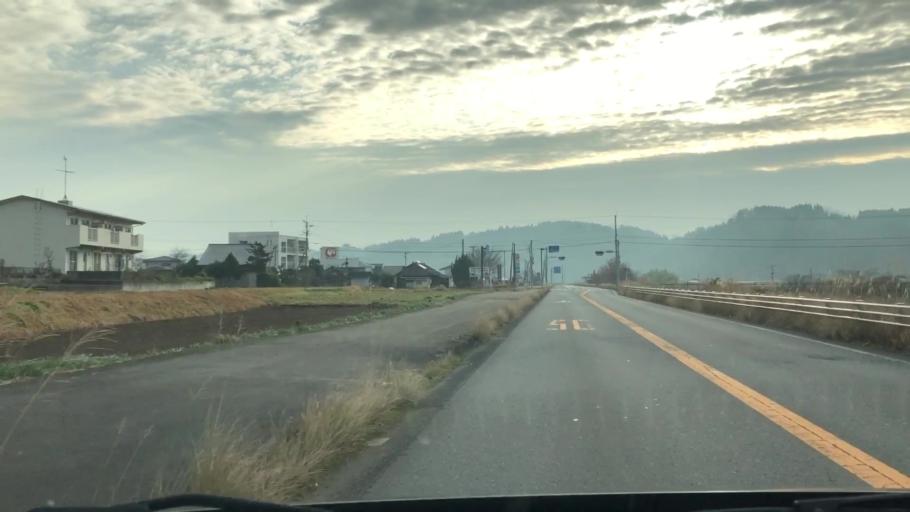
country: JP
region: Oita
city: Takedamachi
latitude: 32.9668
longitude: 131.4799
